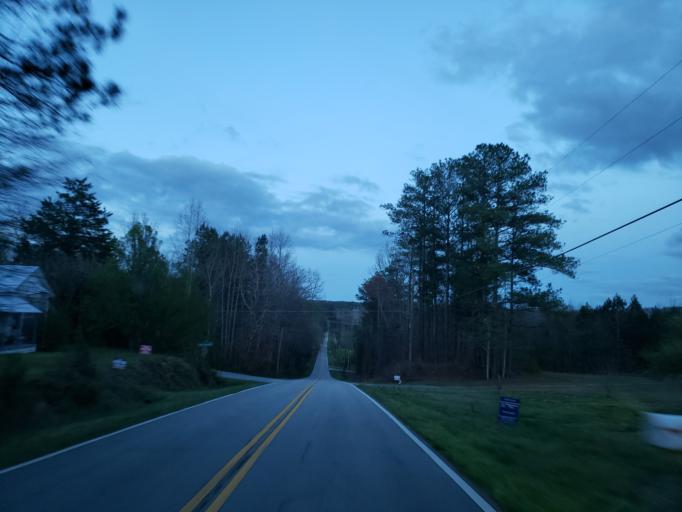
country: US
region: Georgia
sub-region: Paulding County
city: Dallas
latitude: 34.0061
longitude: -84.8992
